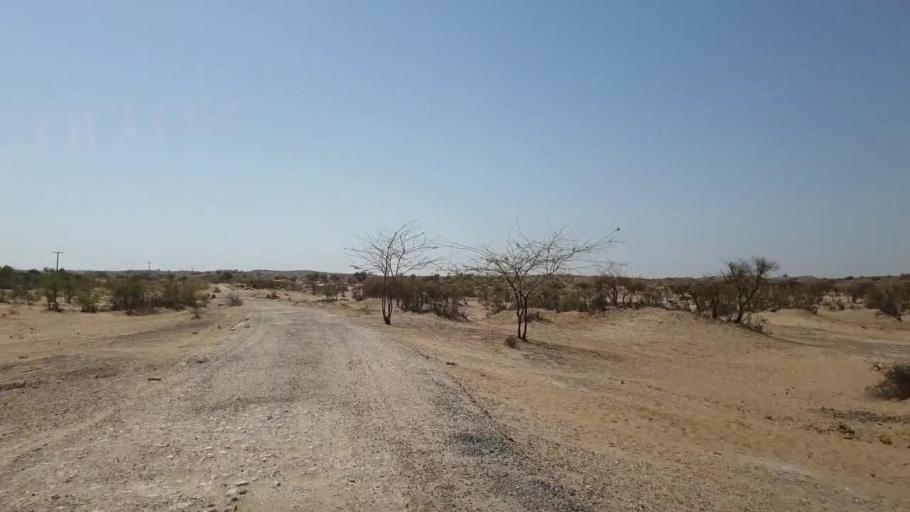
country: PK
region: Sindh
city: Nabisar
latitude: 25.1348
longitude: 69.9179
